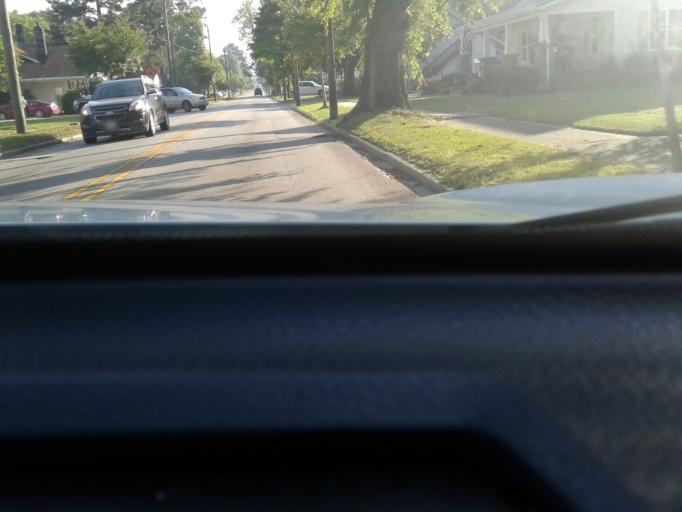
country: US
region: North Carolina
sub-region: Harnett County
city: Dunn
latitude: 35.3133
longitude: -78.6137
